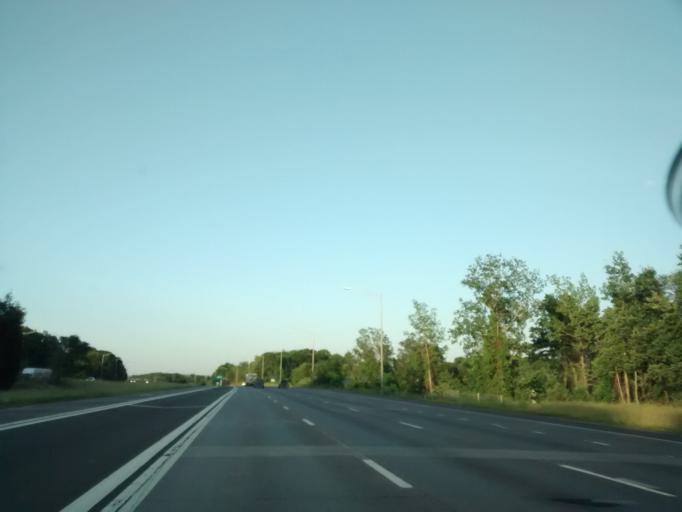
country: US
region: Connecticut
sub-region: Hartford County
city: Manchester
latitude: 41.8031
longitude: -72.5450
